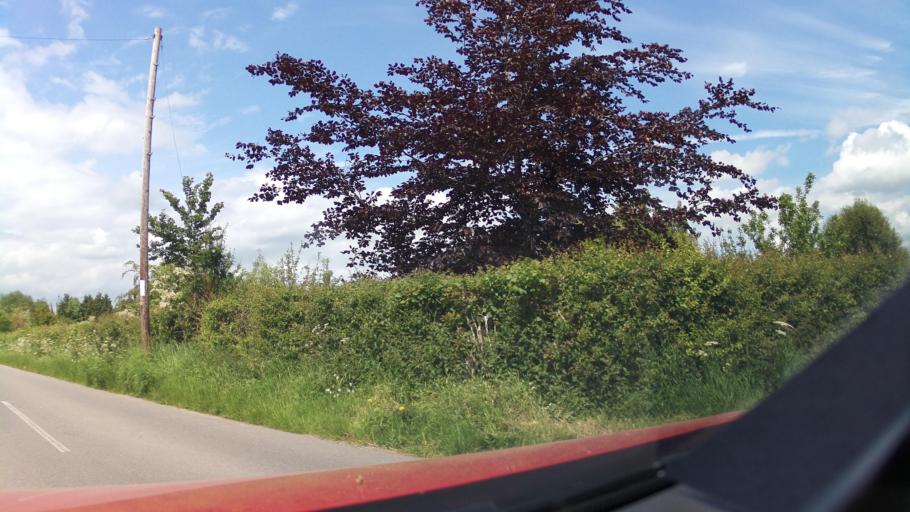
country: GB
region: England
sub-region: Herefordshire
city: Llanrothal
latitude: 51.8534
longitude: -2.8034
